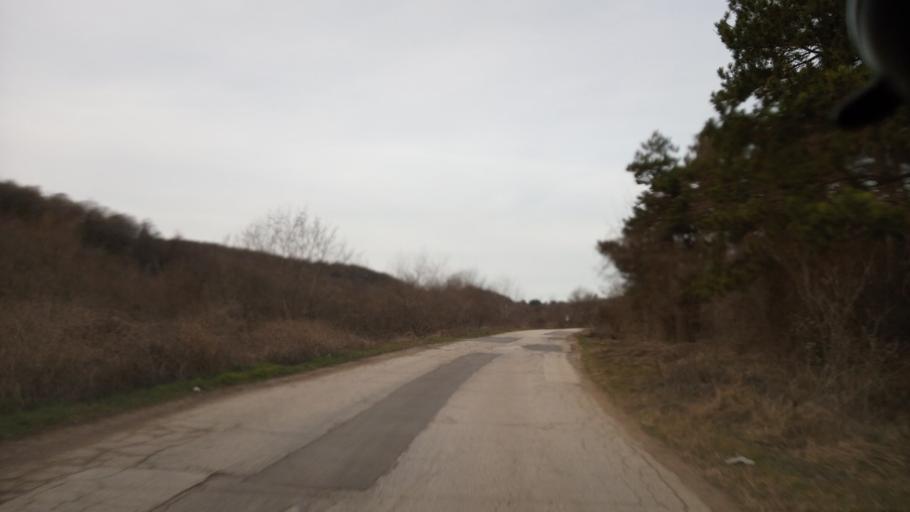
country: BG
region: Pleven
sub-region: Obshtina Belene
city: Belene
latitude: 43.5957
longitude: 24.9904
